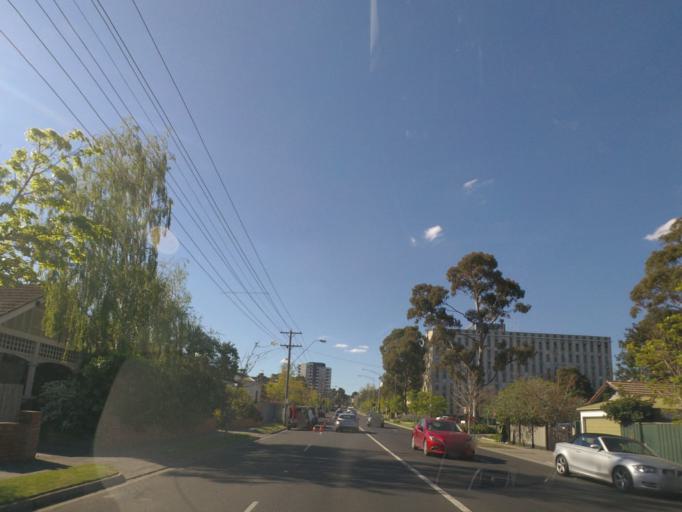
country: AU
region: Victoria
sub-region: Boroondara
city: Kew
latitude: -37.8115
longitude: 145.0282
